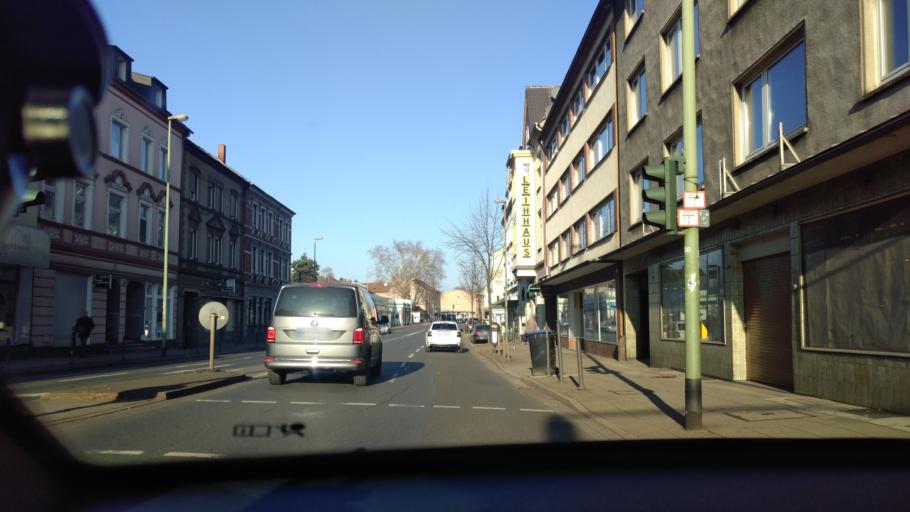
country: DE
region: North Rhine-Westphalia
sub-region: Regierungsbezirk Dusseldorf
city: Essen
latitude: 51.4881
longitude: 7.0093
